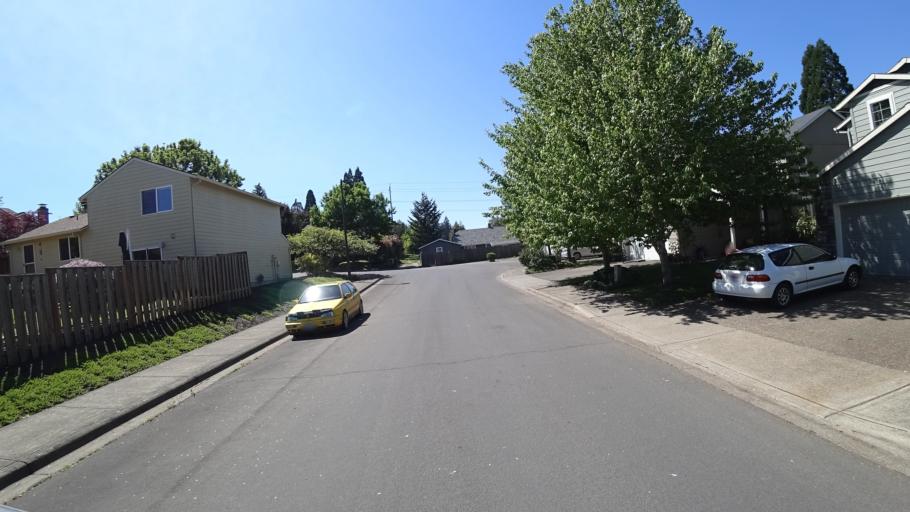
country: US
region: Oregon
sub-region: Washington County
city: Aloha
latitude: 45.4776
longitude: -122.8506
